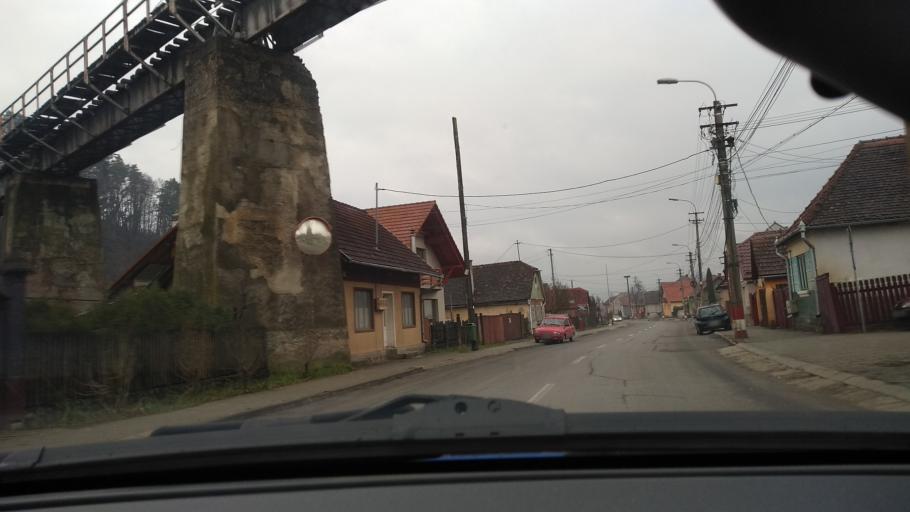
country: RO
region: Mures
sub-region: Oras Sovata
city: Sovata
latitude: 46.5906
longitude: 25.0709
